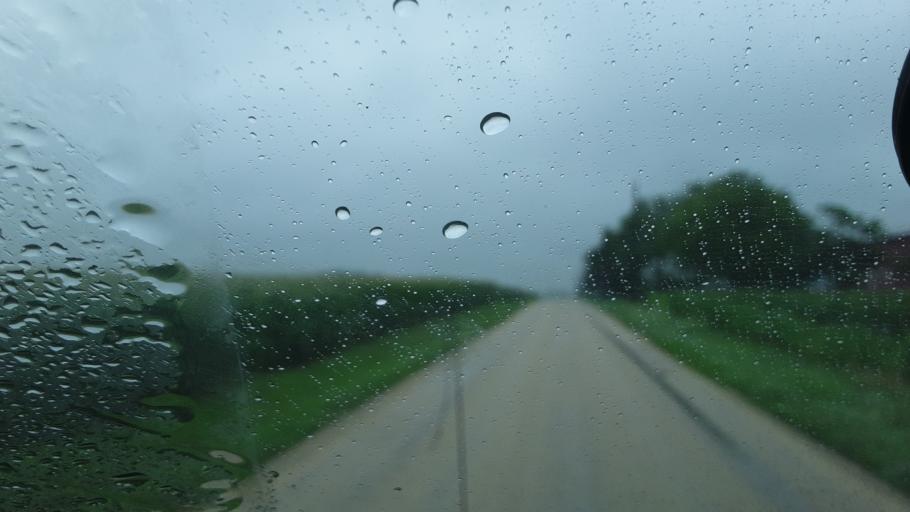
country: US
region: Indiana
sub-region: Adams County
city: Berne
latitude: 40.6876
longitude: -84.9304
